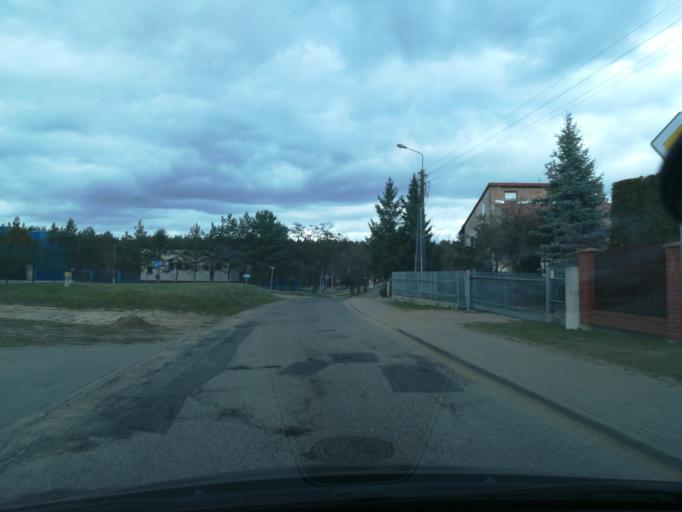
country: PL
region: Kujawsko-Pomorskie
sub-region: Powiat torunski
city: Lubicz Dolny
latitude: 52.9765
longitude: 18.6846
